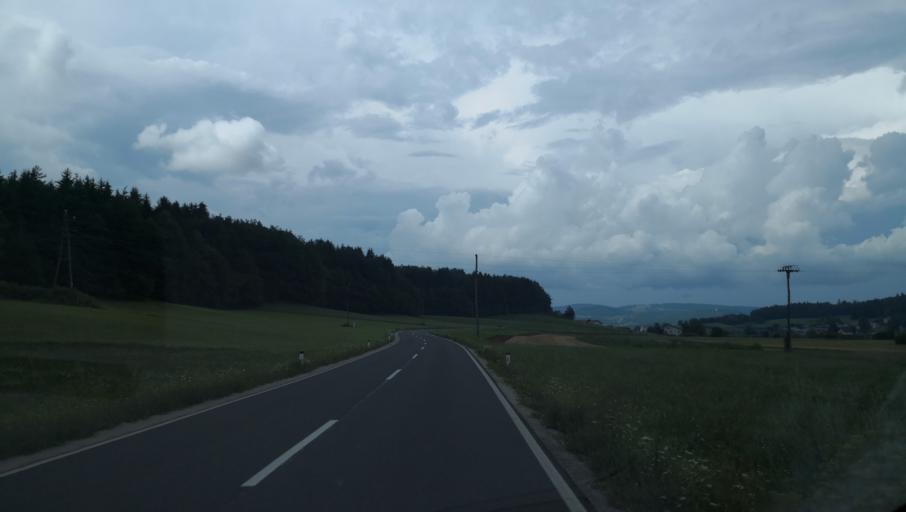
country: SI
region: Ivancna Gorica
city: Ivancna Gorica
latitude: 45.9081
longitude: 14.8006
